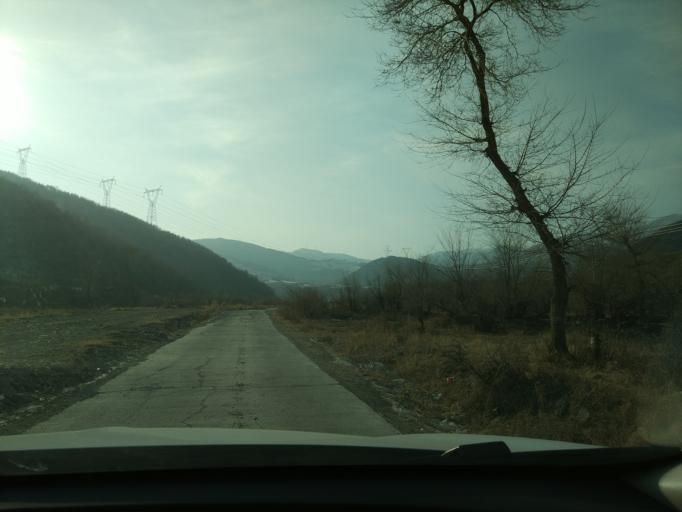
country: CN
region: Hebei
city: Xiwanzi
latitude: 40.8151
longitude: 115.4690
